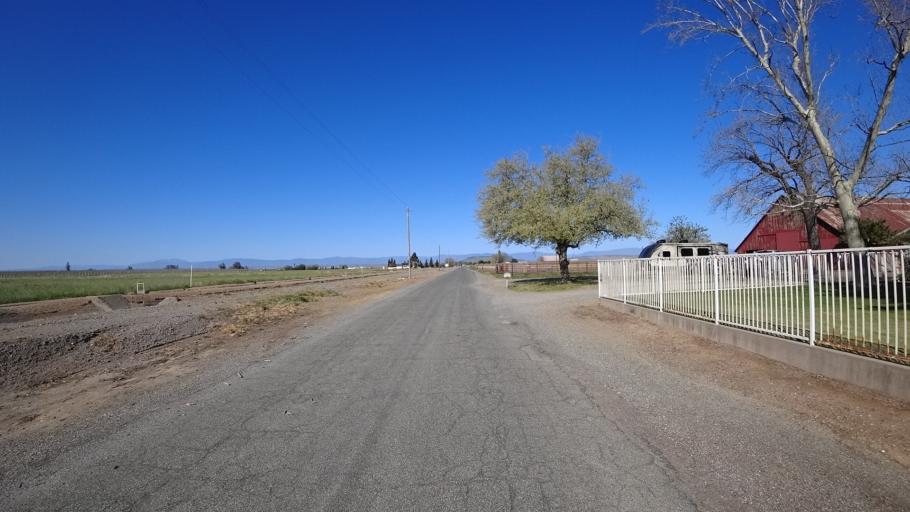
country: US
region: California
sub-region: Glenn County
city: Orland
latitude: 39.7443
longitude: -122.2394
